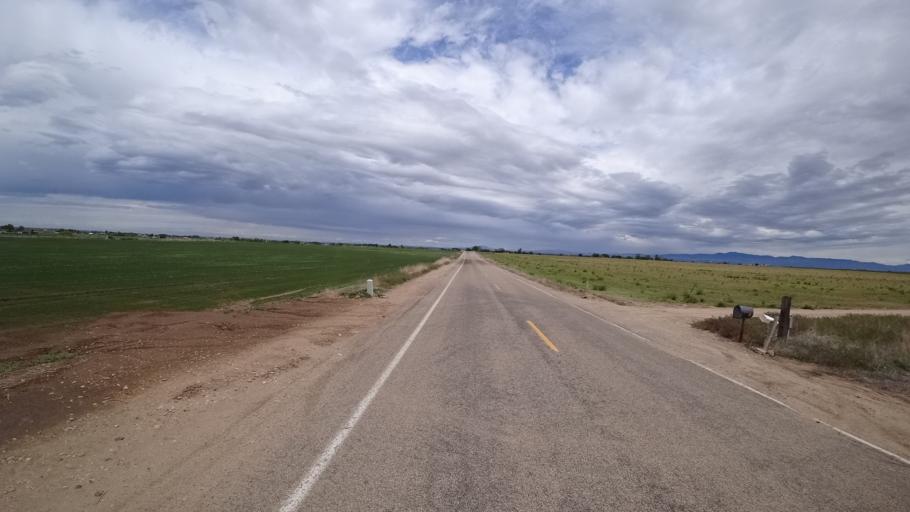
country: US
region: Idaho
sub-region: Ada County
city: Kuna
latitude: 43.4628
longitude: -116.4437
